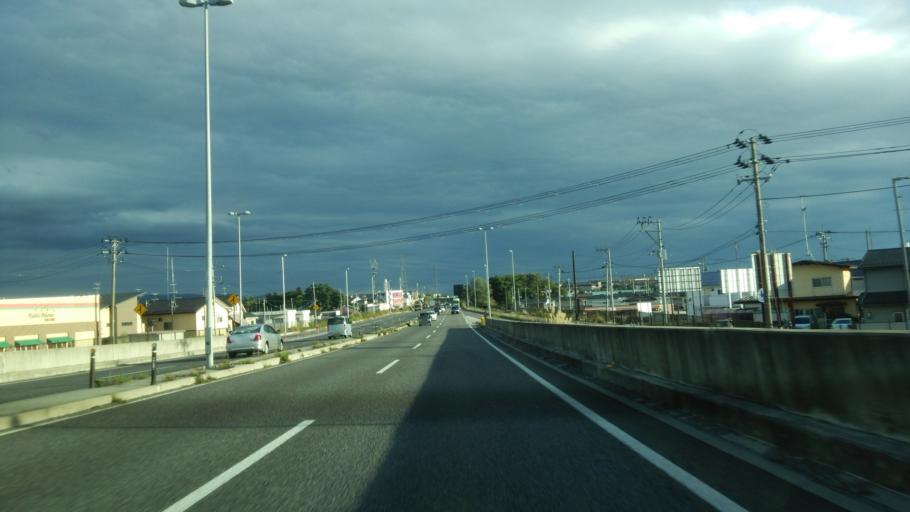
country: JP
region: Fukushima
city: Koriyama
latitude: 37.3840
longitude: 140.3445
